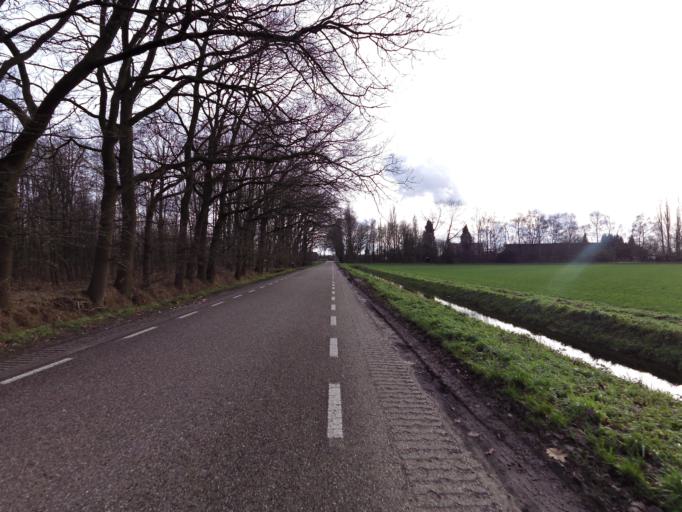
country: NL
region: Gelderland
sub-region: Oude IJsselstreek
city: Wisch
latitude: 51.9675
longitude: 6.4198
